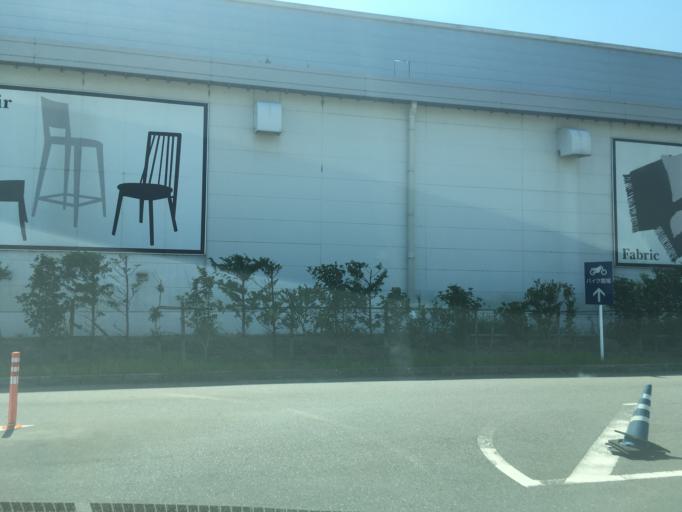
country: JP
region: Chiba
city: Kisarazu
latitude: 35.4335
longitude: 139.9370
